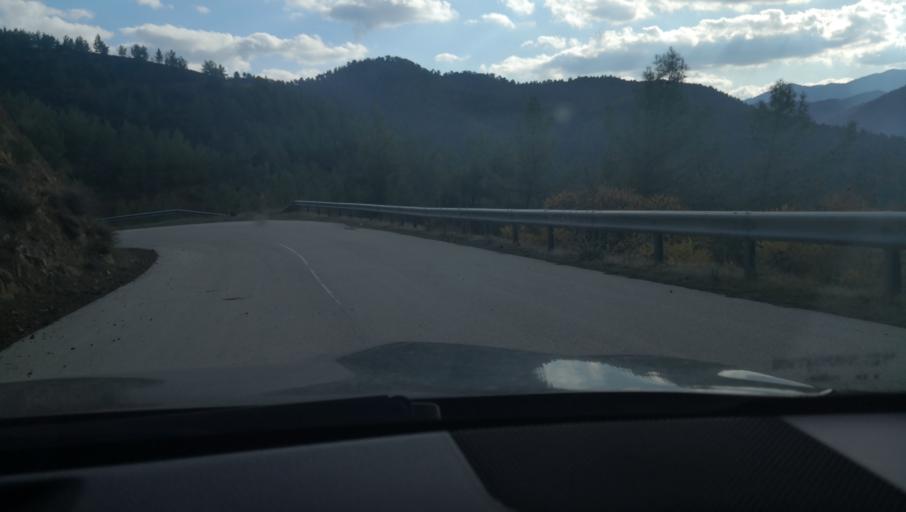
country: CY
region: Lefkosia
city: Lefka
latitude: 35.0604
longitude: 32.7489
